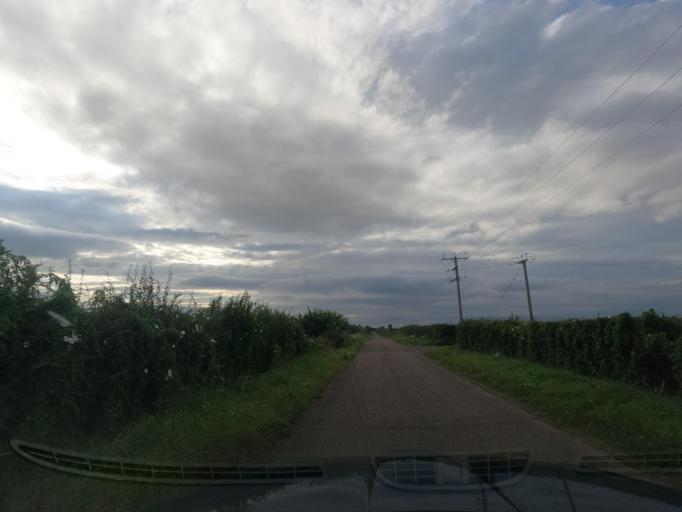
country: GB
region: England
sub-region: Northumberland
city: Ancroft
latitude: 55.7225
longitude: -2.0732
